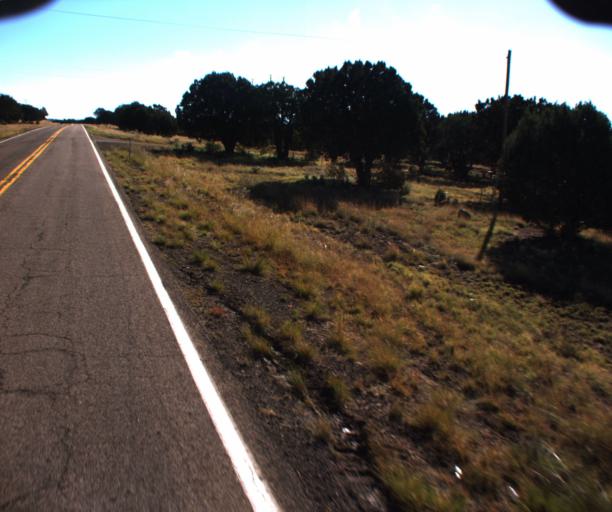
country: US
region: Arizona
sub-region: Navajo County
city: White Mountain Lake
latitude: 34.2898
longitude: -109.8145
